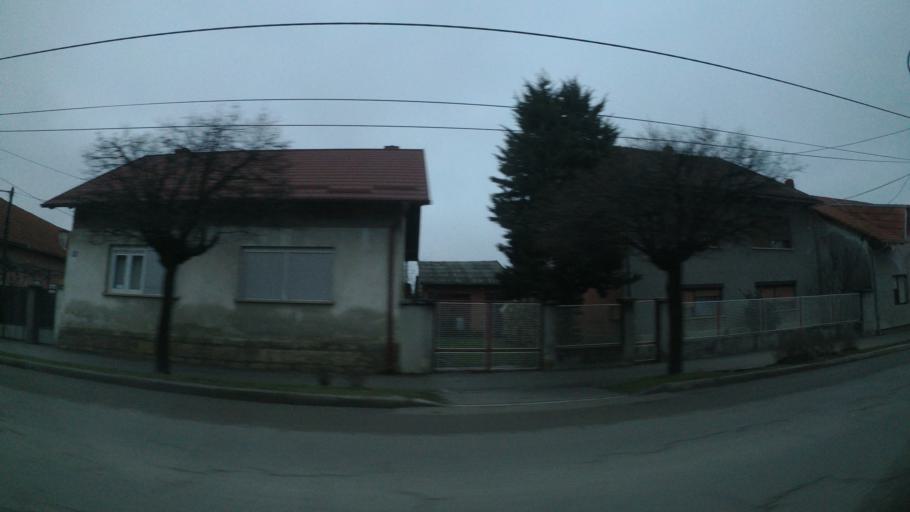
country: HR
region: Sisacko-Moslavacka
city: Petrinja
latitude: 45.4422
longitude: 16.2880
